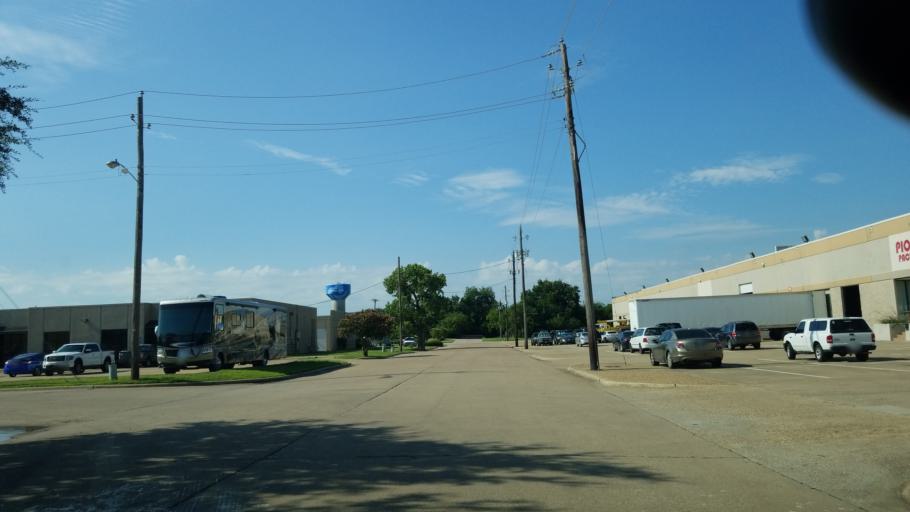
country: US
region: Texas
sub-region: Dallas County
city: Carrollton
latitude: 32.9561
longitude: -96.9193
